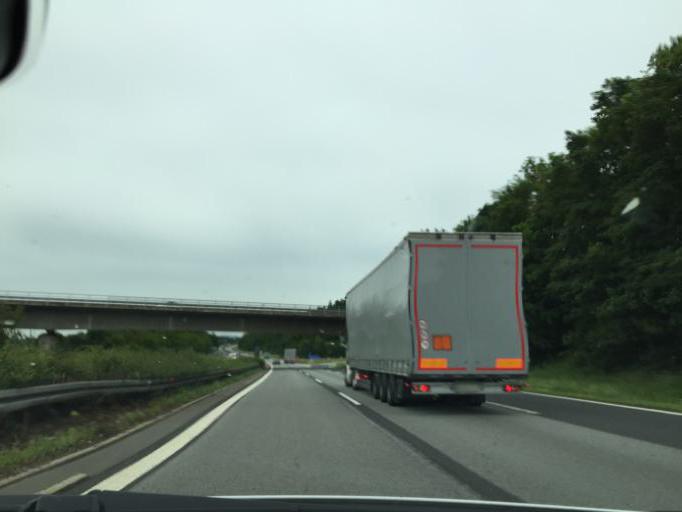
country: DE
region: Bavaria
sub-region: Regierungsbezirk Unterfranken
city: Gadheim
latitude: 50.0215
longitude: 10.3242
